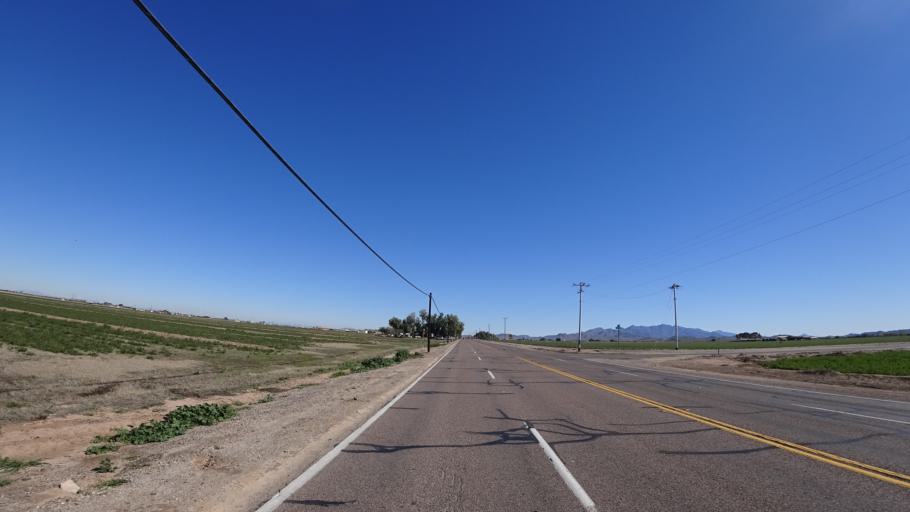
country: US
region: Arizona
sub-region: Maricopa County
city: Buckeye
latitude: 33.3776
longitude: -112.4954
